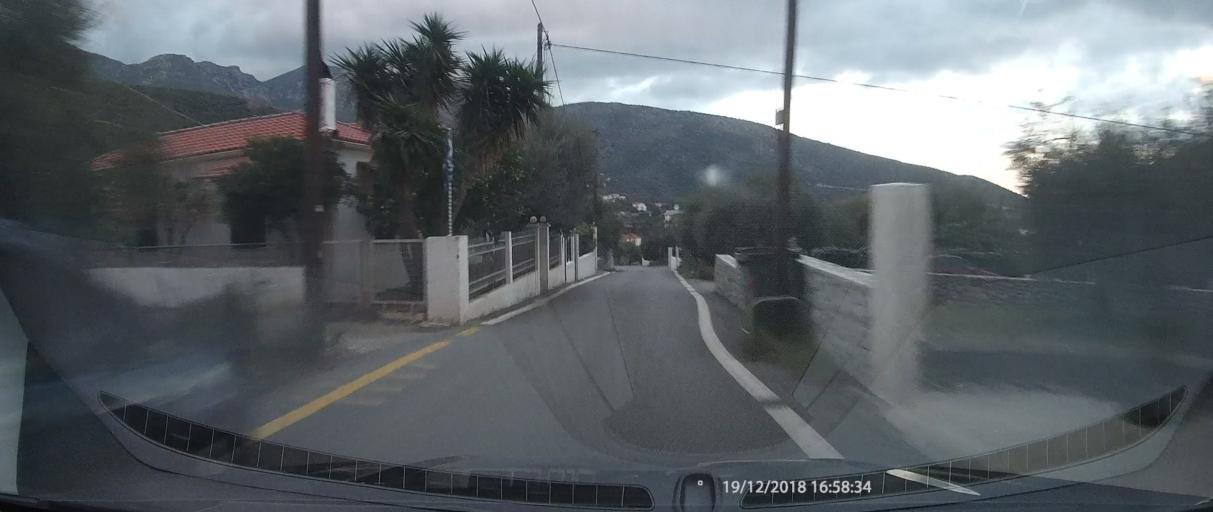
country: GR
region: Peloponnese
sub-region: Nomos Lakonias
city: Sykea
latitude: 36.9703
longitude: 22.9897
